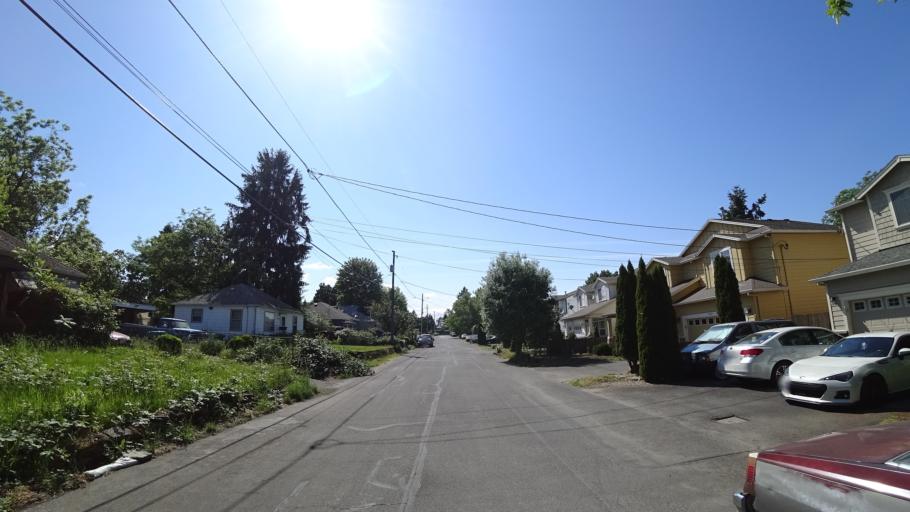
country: US
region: Oregon
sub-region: Multnomah County
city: Lents
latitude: 45.5594
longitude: -122.5697
